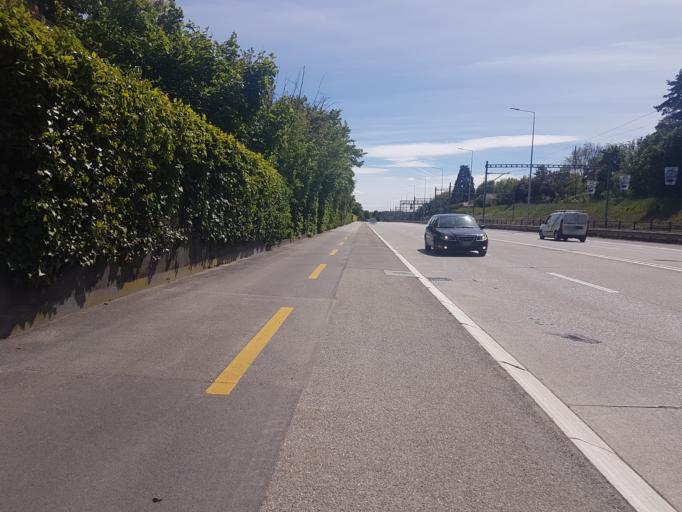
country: CH
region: Geneva
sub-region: Geneva
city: Bellevue
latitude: 46.2680
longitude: 6.1641
